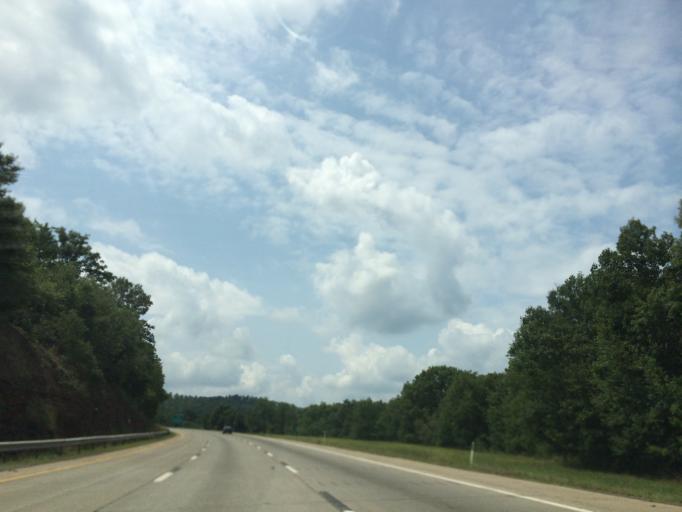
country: US
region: Pennsylvania
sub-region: Luzerne County
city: Harleigh
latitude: 41.0718
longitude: -75.9824
